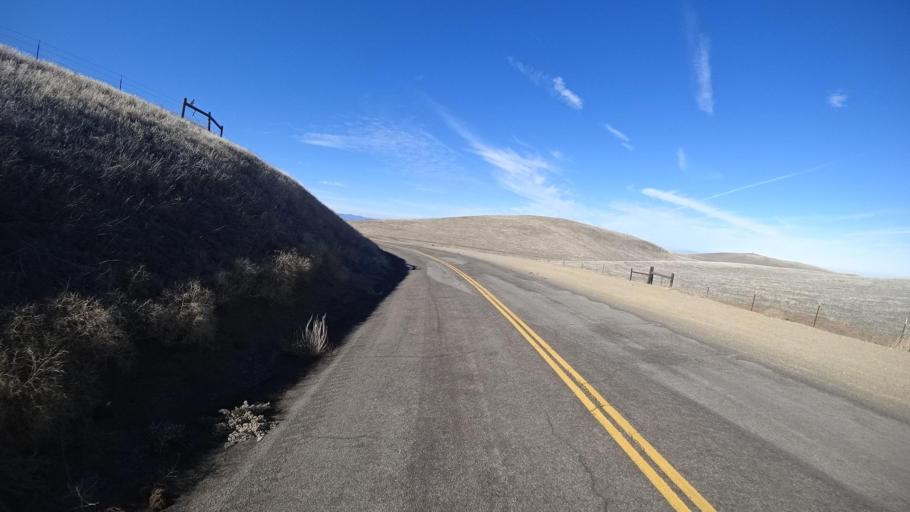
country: US
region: California
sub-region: Kern County
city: Maricopa
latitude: 34.9077
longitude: -119.3889
